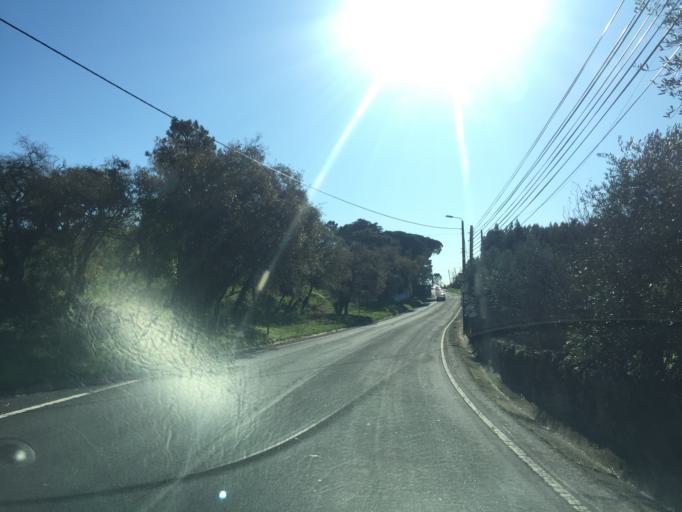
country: PT
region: Lisbon
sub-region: Sintra
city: Belas
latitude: 38.7946
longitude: -9.2678
